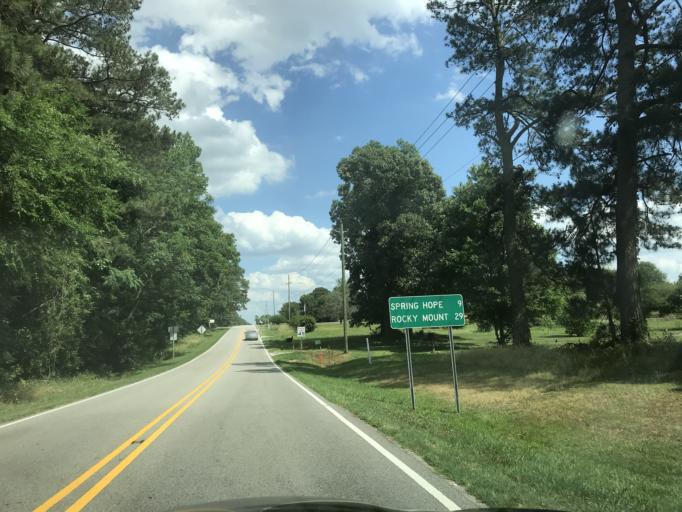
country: US
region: North Carolina
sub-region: Nash County
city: Spring Hope
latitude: 35.9525
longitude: -78.2435
